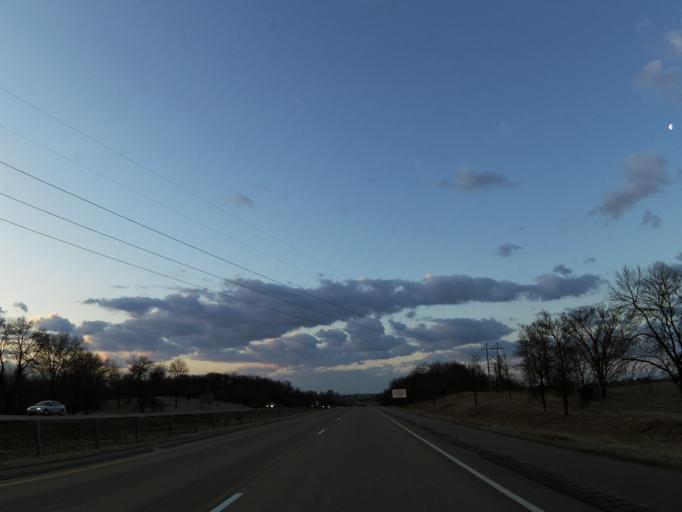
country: US
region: Minnesota
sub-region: Scott County
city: Elko New Market
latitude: 44.5188
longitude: -93.2923
